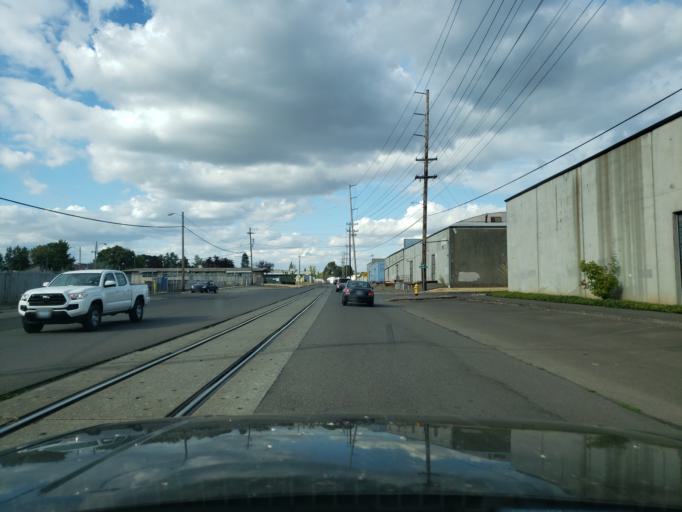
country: US
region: Oregon
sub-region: Marion County
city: Salem
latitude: 44.9527
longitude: -123.0361
